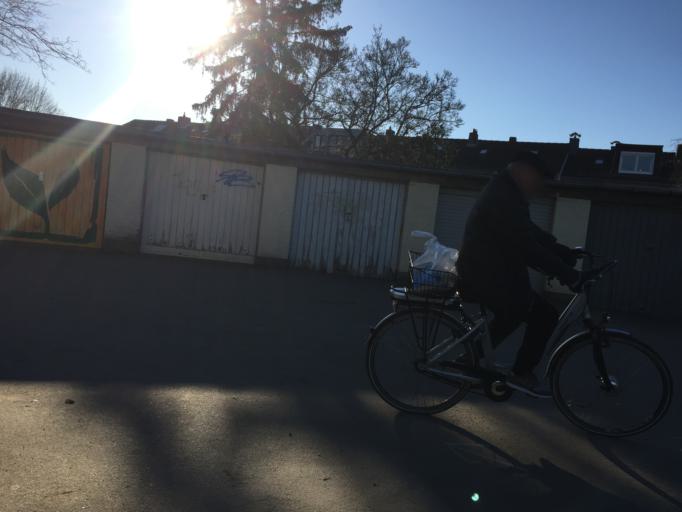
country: DE
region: Hesse
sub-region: Regierungsbezirk Darmstadt
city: Frankfurt am Main
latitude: 50.1573
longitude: 8.6664
